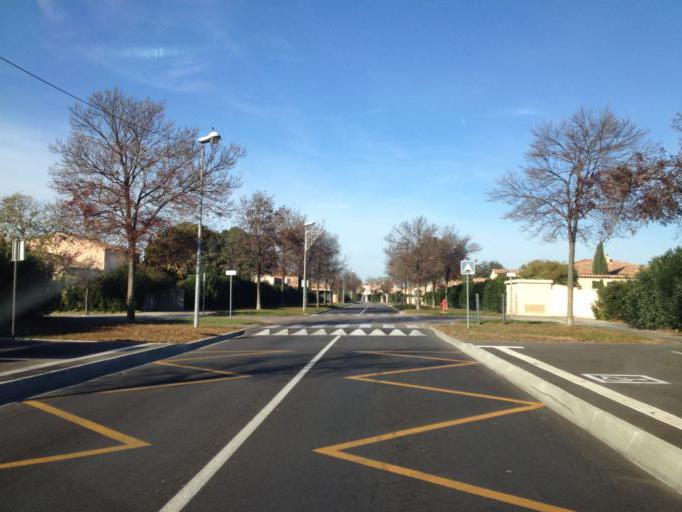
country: FR
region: Provence-Alpes-Cote d'Azur
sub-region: Departement des Bouches-du-Rhone
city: Istres
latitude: 43.5036
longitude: 4.9702
